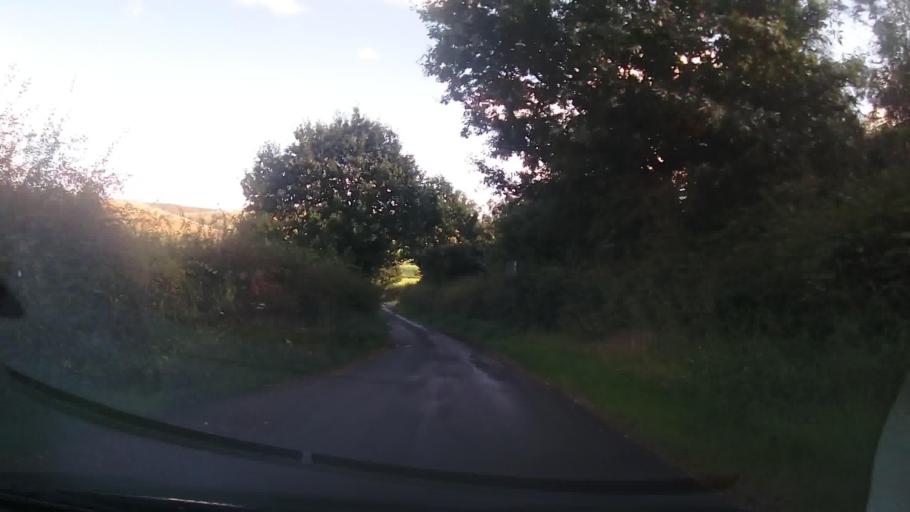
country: GB
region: England
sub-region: Shropshire
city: Norbury
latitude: 52.5658
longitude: -2.9016
